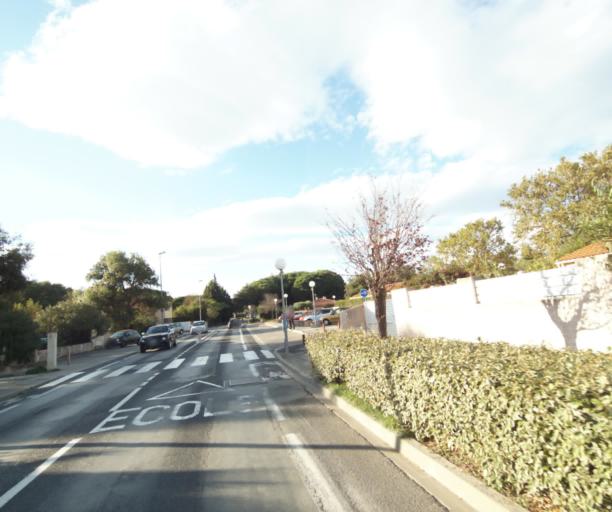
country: FR
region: Languedoc-Roussillon
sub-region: Departement des Pyrenees-Orientales
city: Argelers
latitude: 42.5524
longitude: 3.0284
